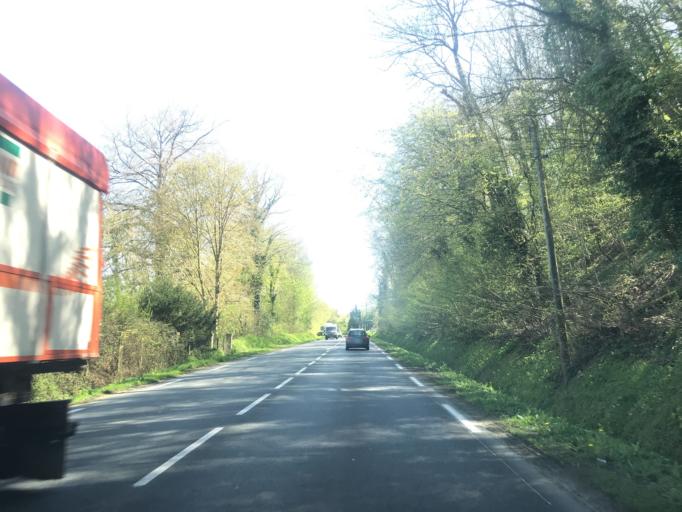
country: FR
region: Haute-Normandie
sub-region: Departement de l'Eure
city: Fleury-sur-Andelle
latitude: 49.3550
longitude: 1.3615
